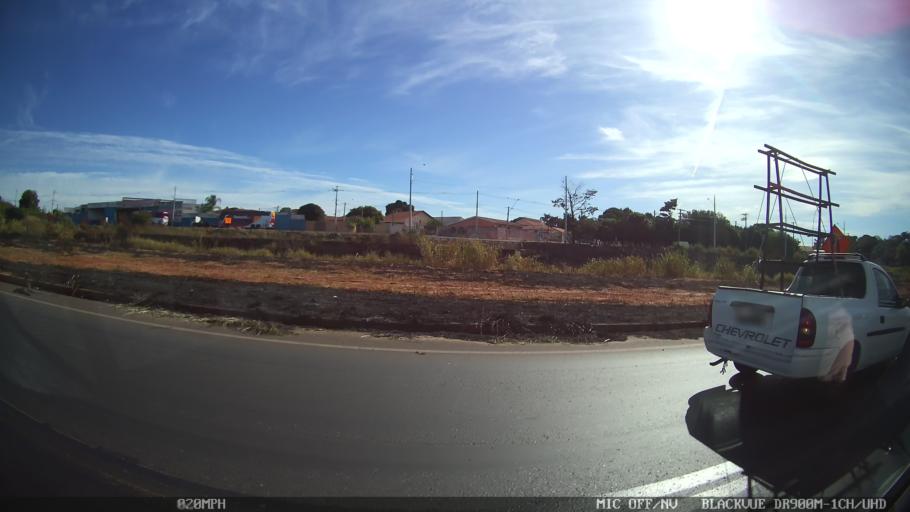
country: BR
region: Sao Paulo
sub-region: Sao Jose Do Rio Preto
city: Sao Jose do Rio Preto
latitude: -20.7828
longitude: -49.3528
